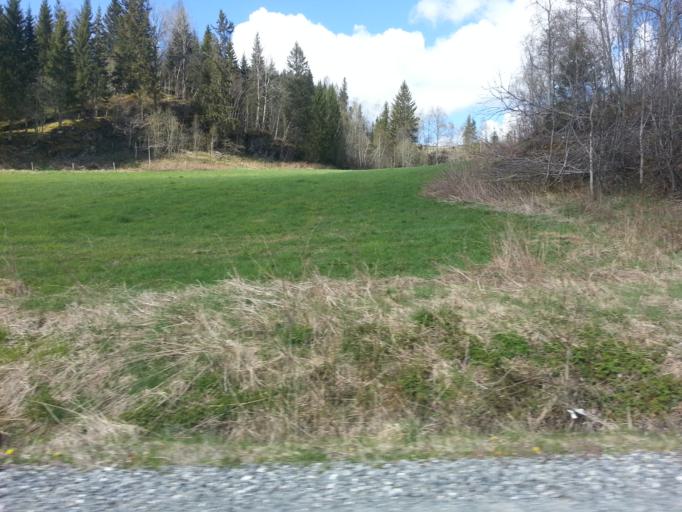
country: NO
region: Nord-Trondelag
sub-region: Levanger
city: Skogn
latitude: 63.6377
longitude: 11.2392
